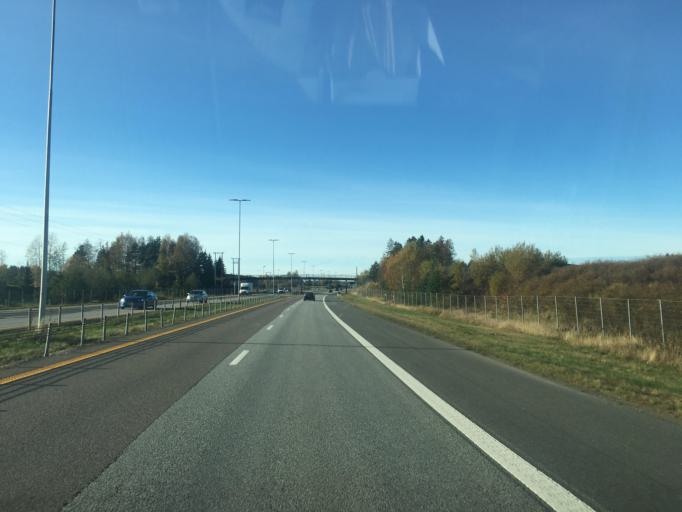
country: NO
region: Ostfold
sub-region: Rade
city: Karlshus
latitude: 59.3565
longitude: 10.8539
